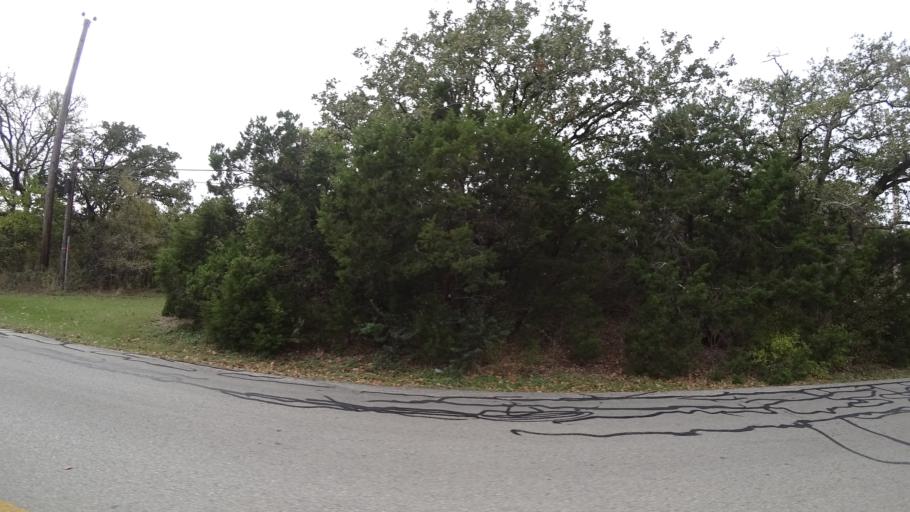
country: US
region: Texas
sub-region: Travis County
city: Shady Hollow
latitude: 30.1386
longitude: -97.8748
